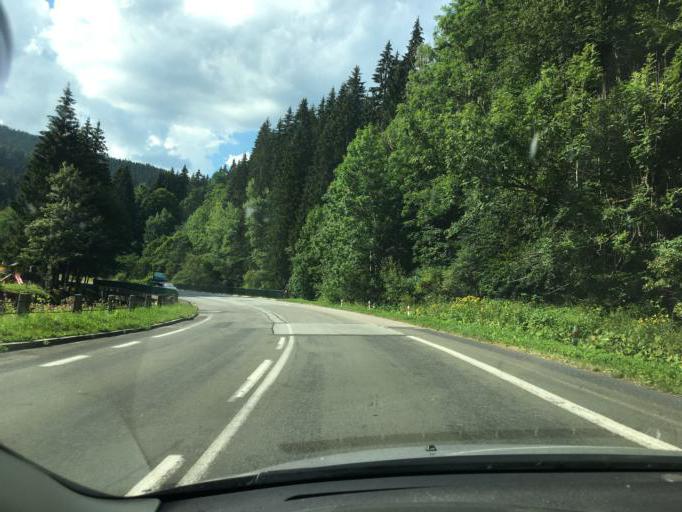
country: CZ
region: Kralovehradecky
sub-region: Okres Trutnov
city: Spindleruv Mlyn
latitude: 50.7000
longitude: 15.5877
